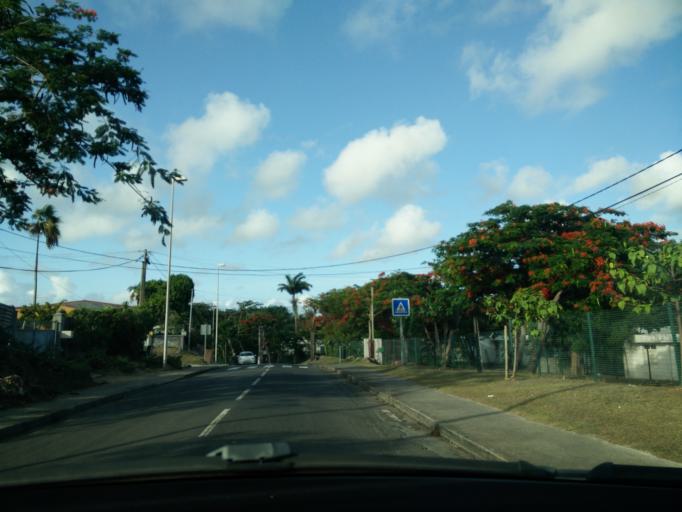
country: GP
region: Guadeloupe
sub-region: Guadeloupe
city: Le Moule
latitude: 16.3259
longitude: -61.3440
